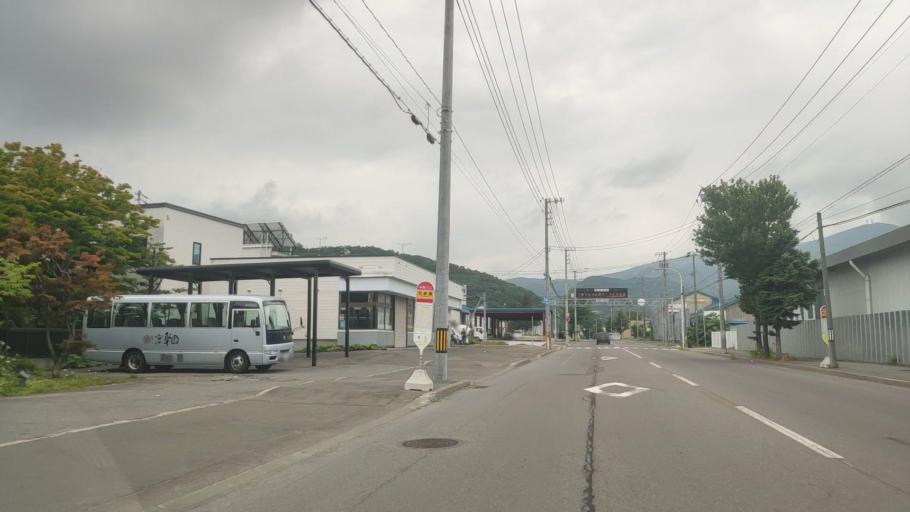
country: JP
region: Hokkaido
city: Otaru
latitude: 43.1652
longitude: 141.0494
